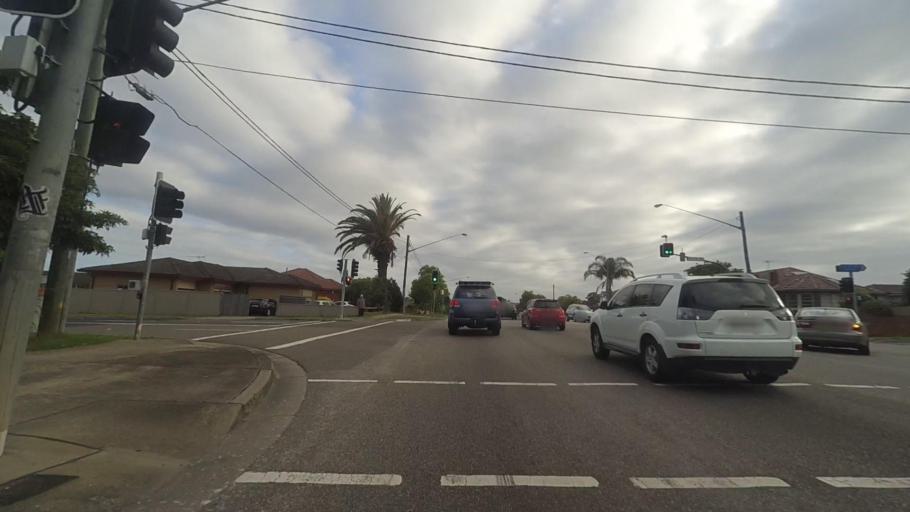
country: AU
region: New South Wales
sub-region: Bankstown
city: Padstow
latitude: -33.9537
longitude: 151.0383
